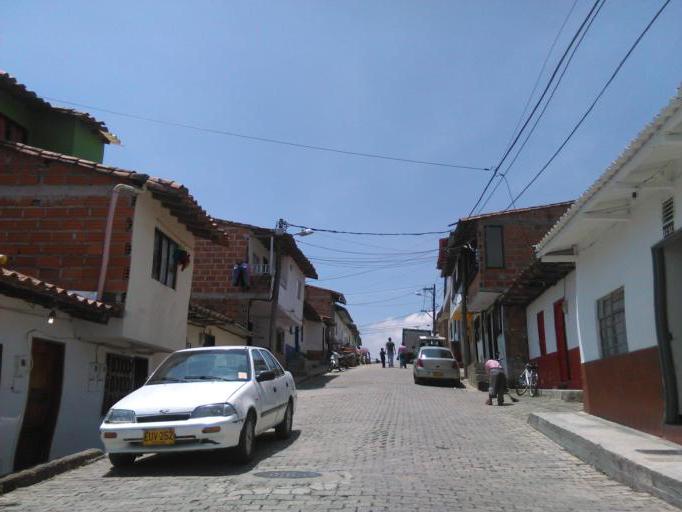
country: CO
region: Antioquia
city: La Union
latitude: 5.9731
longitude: -75.3633
